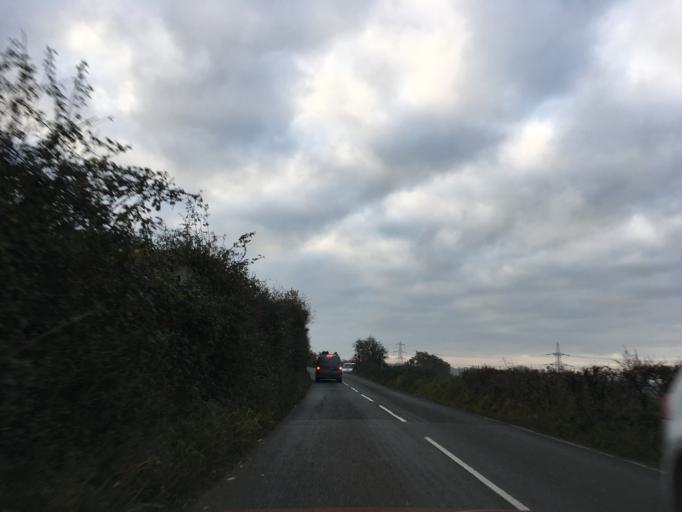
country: GB
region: England
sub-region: South Gloucestershire
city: Yate
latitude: 51.5316
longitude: -2.4381
